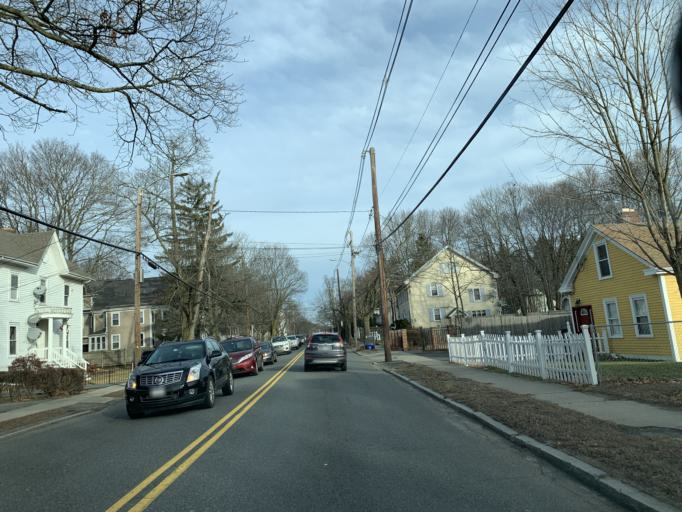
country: US
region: Massachusetts
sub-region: Essex County
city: Saugus
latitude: 42.4645
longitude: -71.0153
